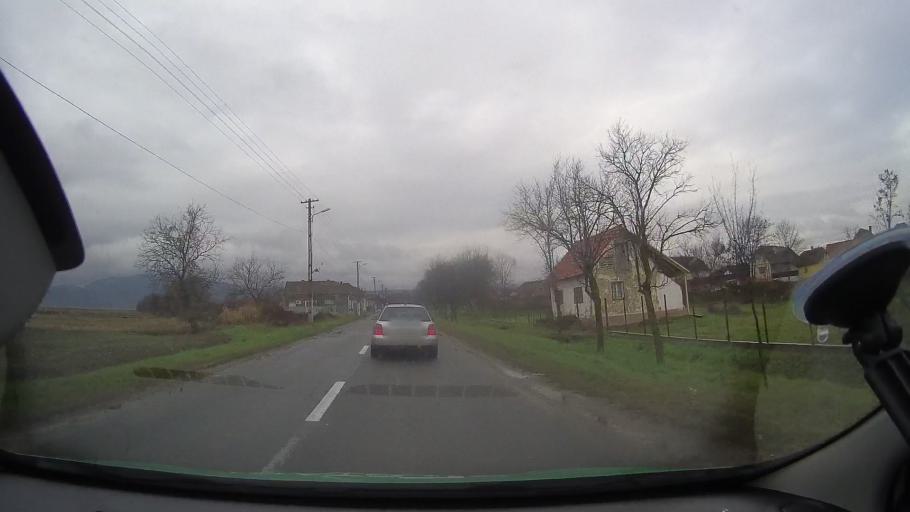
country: RO
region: Arad
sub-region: Comuna Buteni
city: Buteni
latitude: 46.3336
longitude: 22.1262
